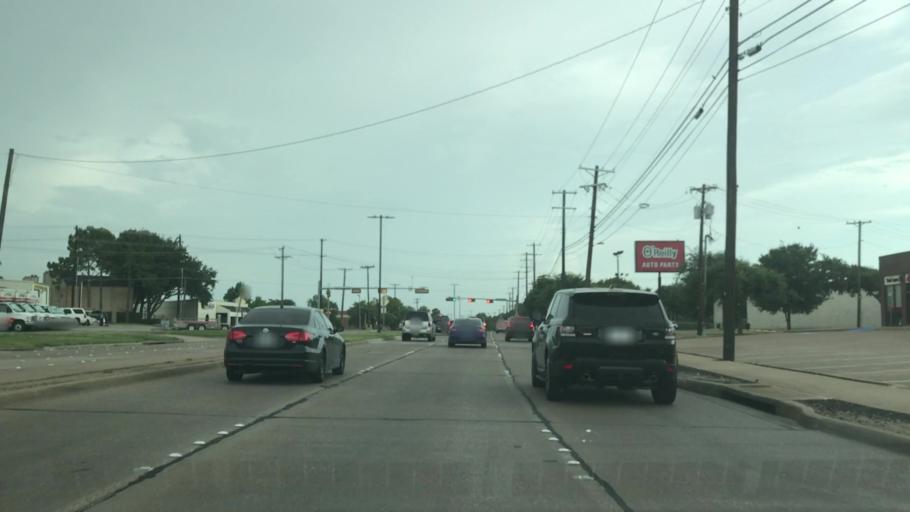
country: US
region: Texas
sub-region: Dallas County
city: Rowlett
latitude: 32.8630
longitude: -96.6037
